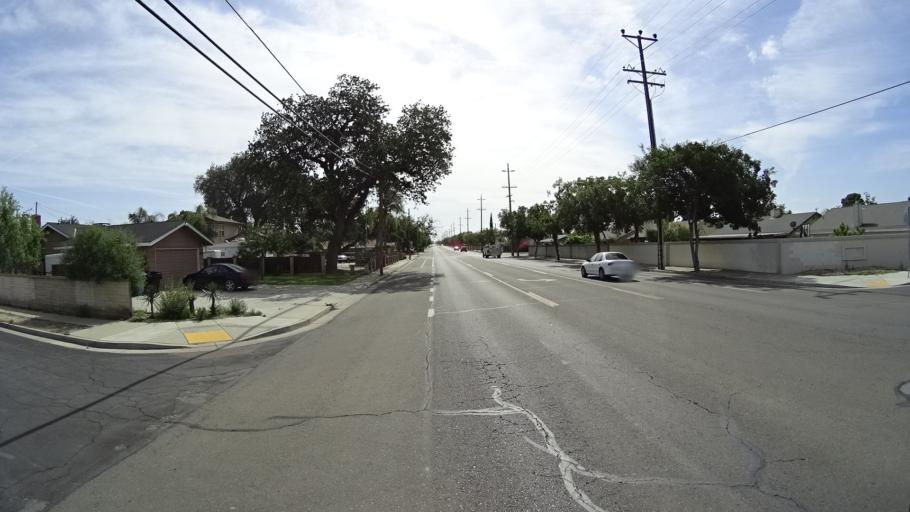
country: US
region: California
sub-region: Kings County
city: Hanford
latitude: 36.3135
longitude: -119.6650
